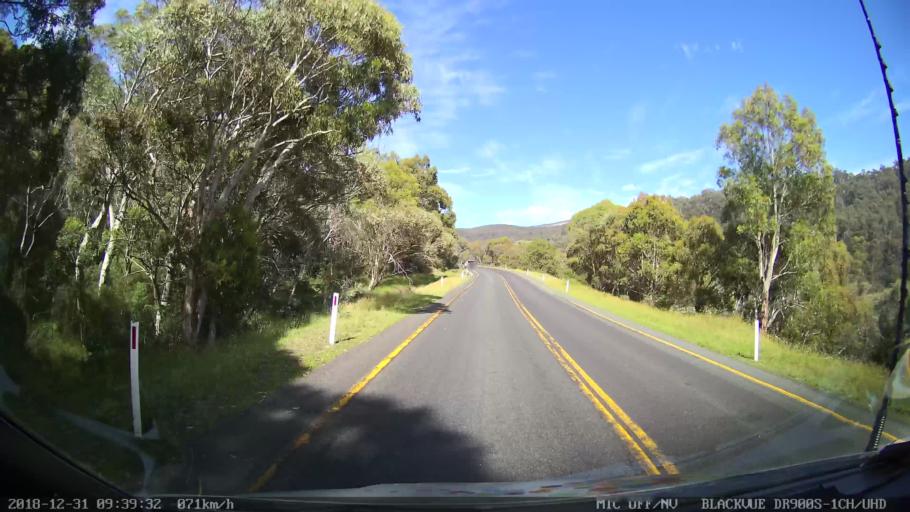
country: AU
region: New South Wales
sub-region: Snowy River
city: Jindabyne
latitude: -36.4794
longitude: 148.3536
